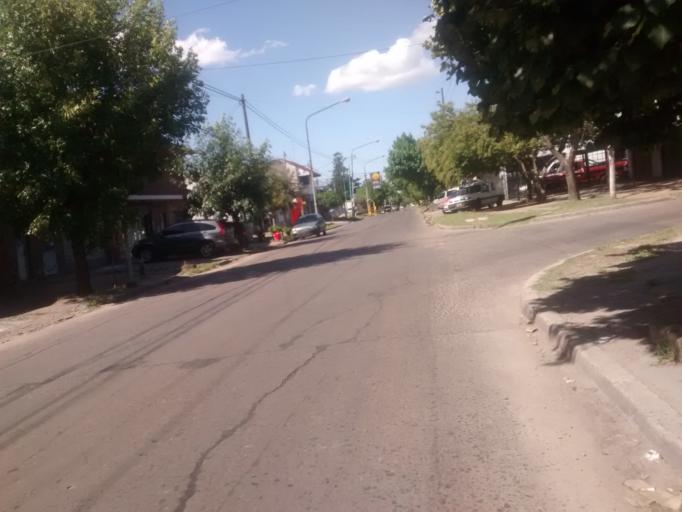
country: AR
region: Buenos Aires
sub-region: Partido de La Plata
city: La Plata
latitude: -34.9295
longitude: -57.9112
